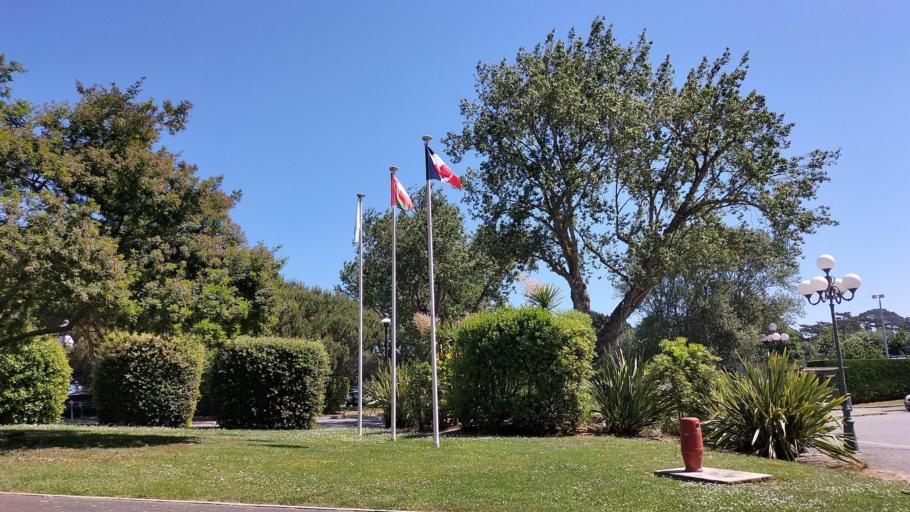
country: FR
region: Brittany
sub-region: Departement d'Ille-et-Vilaine
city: Dinard
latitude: 48.6377
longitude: -2.0751
